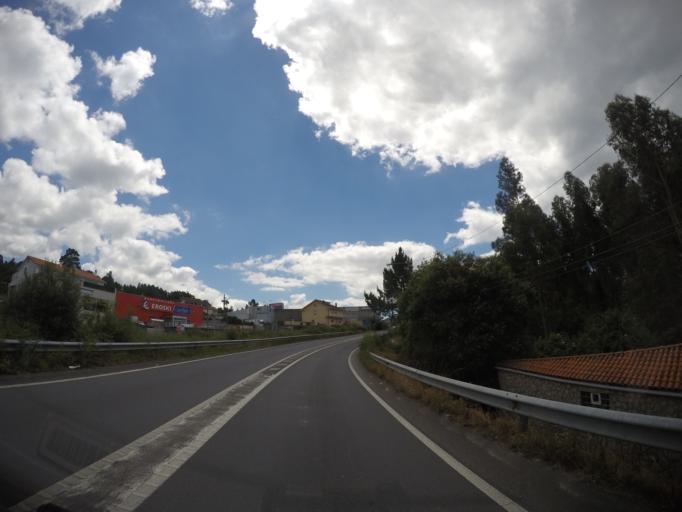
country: MX
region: Guanajuato
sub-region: Celaya
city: Roque
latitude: 20.5595
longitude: -100.8370
